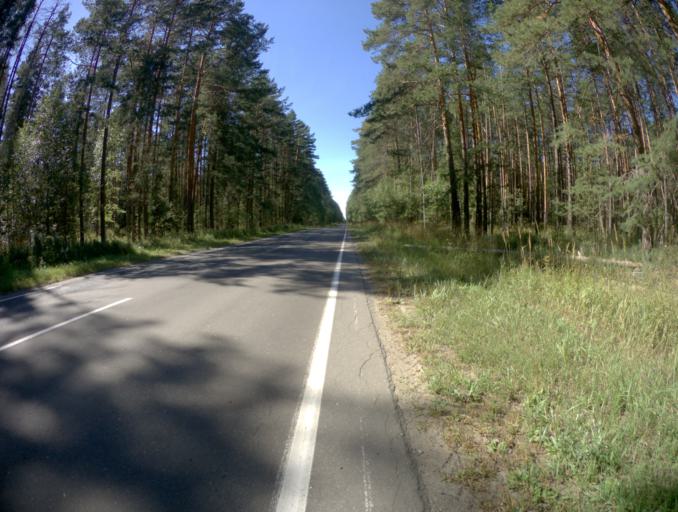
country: RU
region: Vladimir
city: Zolotkovo
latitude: 55.6192
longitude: 41.0200
